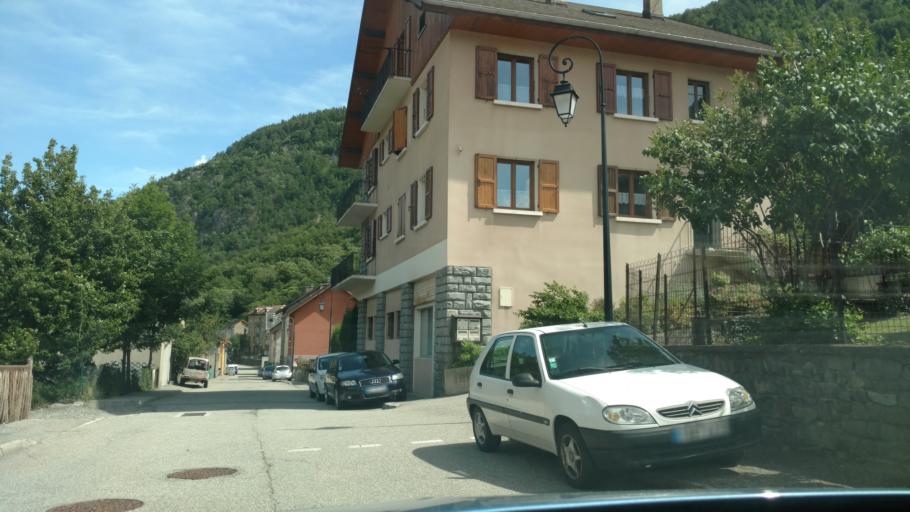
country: FR
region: Rhone-Alpes
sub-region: Departement de la Savoie
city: Villargondran
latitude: 45.2470
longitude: 6.4028
